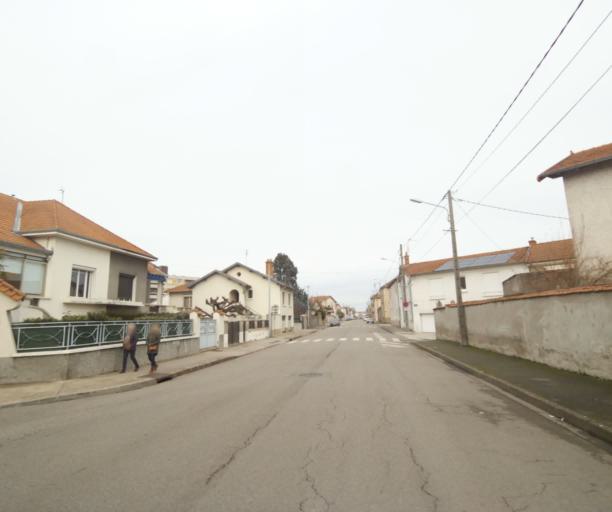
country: FR
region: Rhone-Alpes
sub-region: Departement de la Loire
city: Riorges
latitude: 46.0413
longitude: 4.0556
